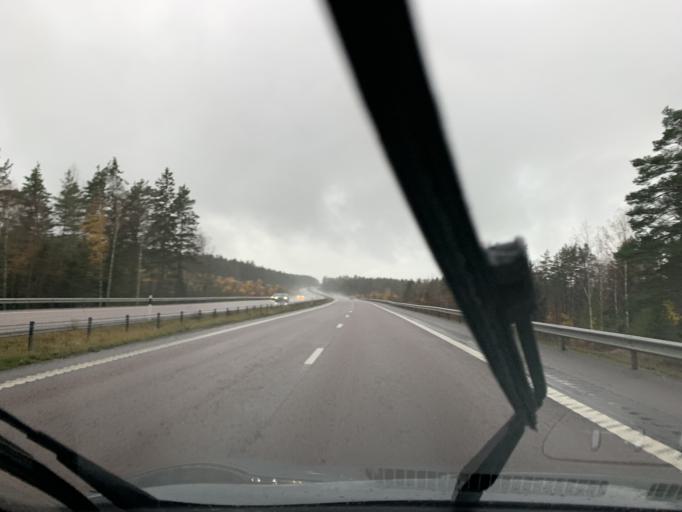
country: SE
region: Soedermanland
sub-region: Nykopings Kommun
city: Olstorp
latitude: 58.7565
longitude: 16.6179
